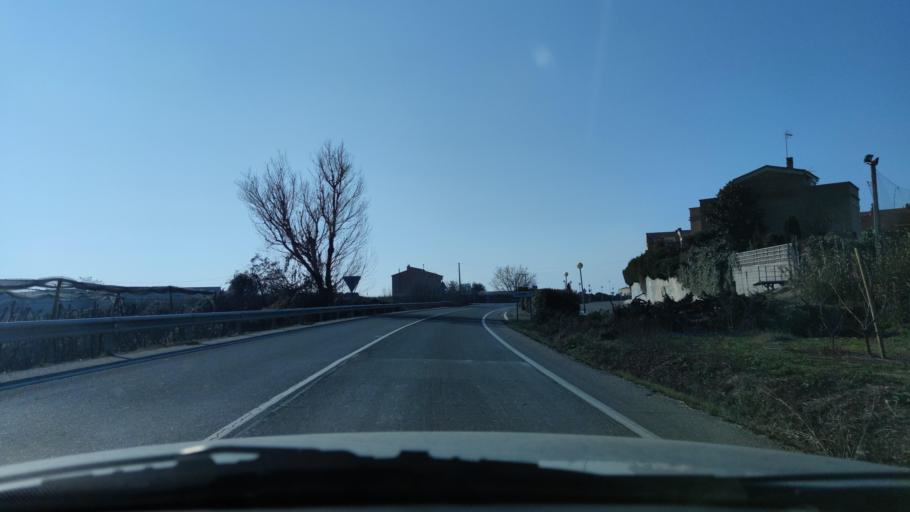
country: ES
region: Catalonia
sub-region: Provincia de Lleida
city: Torrefarrera
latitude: 41.6939
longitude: 0.6361
